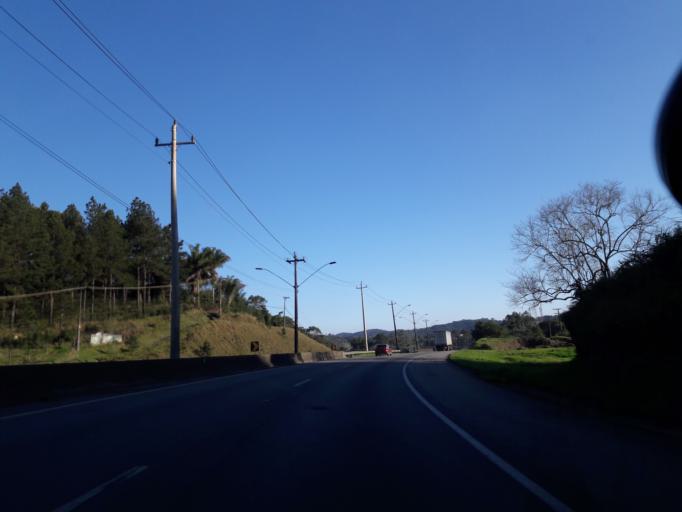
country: BR
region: Sao Paulo
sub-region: Sao Lourenco Da Serra
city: Sao Lourenco da Serra
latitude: -23.9148
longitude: -46.9892
